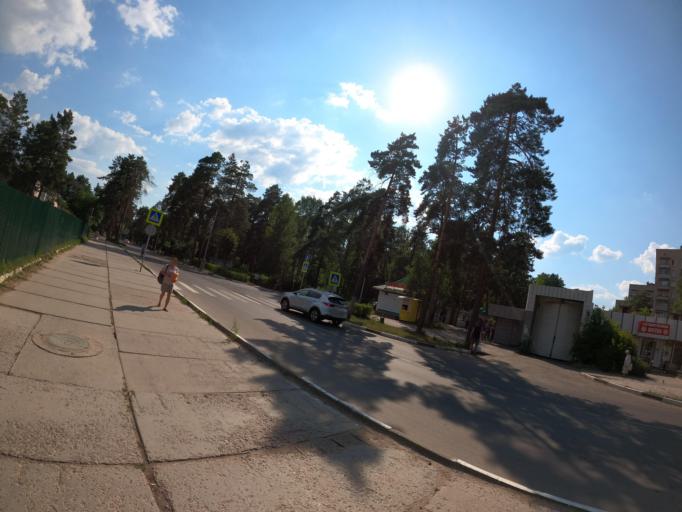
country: RU
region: Moskovskaya
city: Protvino
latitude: 54.8652
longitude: 37.2150
